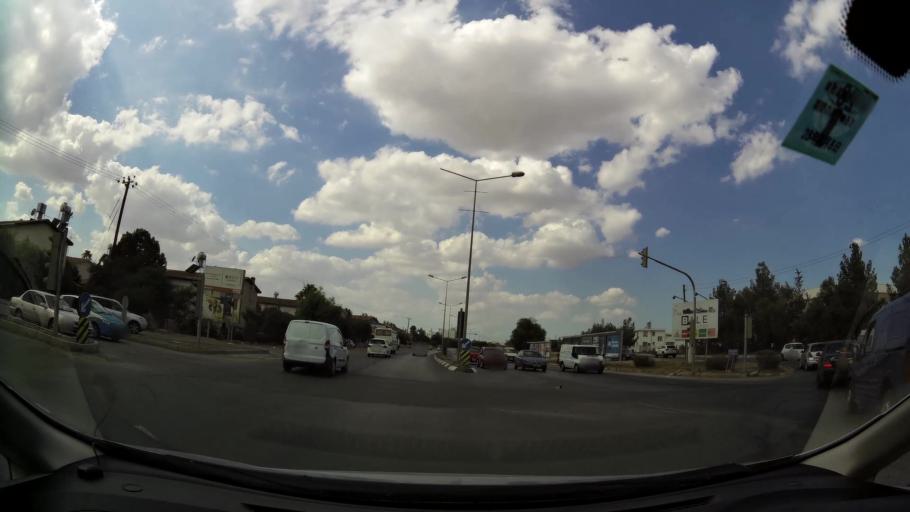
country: CY
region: Lefkosia
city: Nicosia
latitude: 35.2089
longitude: 33.3523
